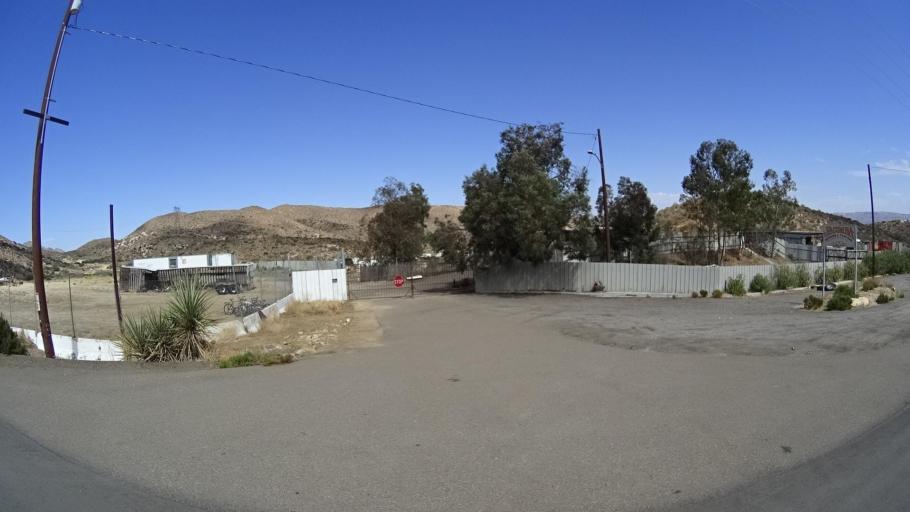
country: MX
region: Baja California
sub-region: Tecate
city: Cereso del Hongo
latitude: 32.6410
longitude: -116.2294
